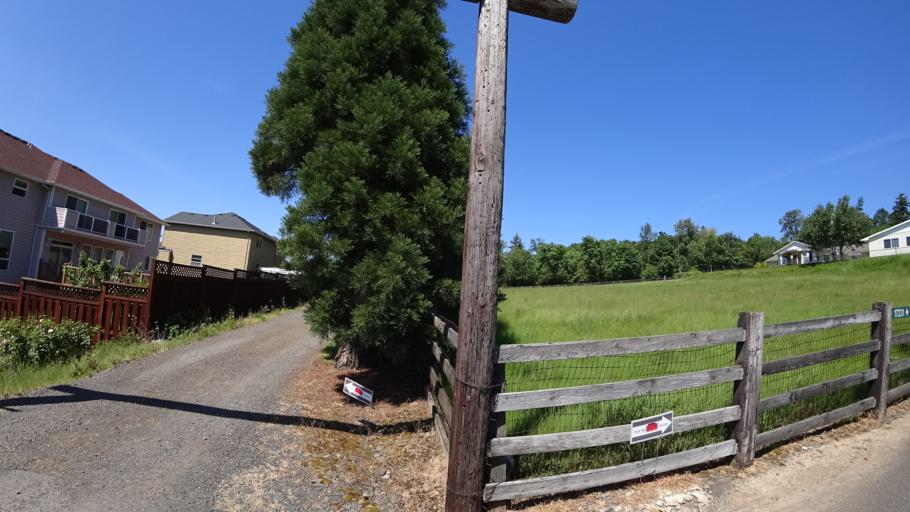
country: US
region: Oregon
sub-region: Clackamas County
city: Happy Valley
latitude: 45.4793
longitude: -122.4852
